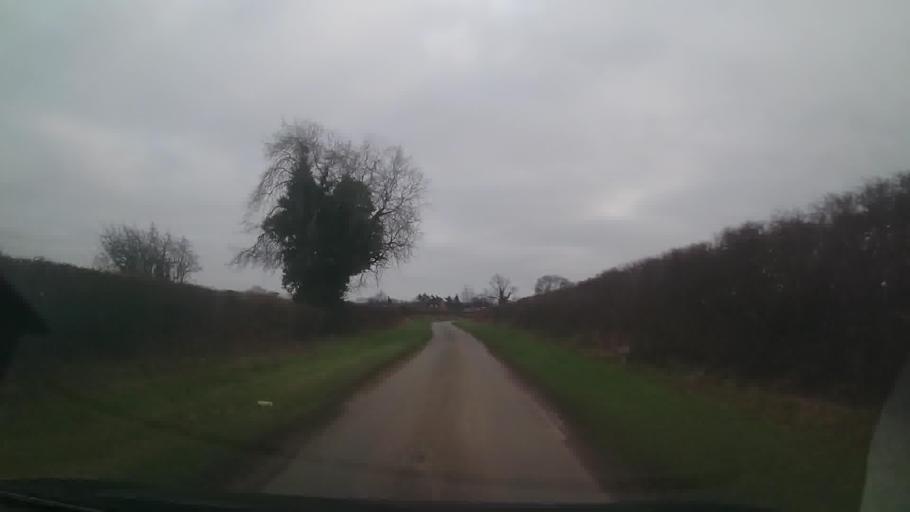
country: GB
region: England
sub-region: Shropshire
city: Petton
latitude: 52.7969
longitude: -2.8294
